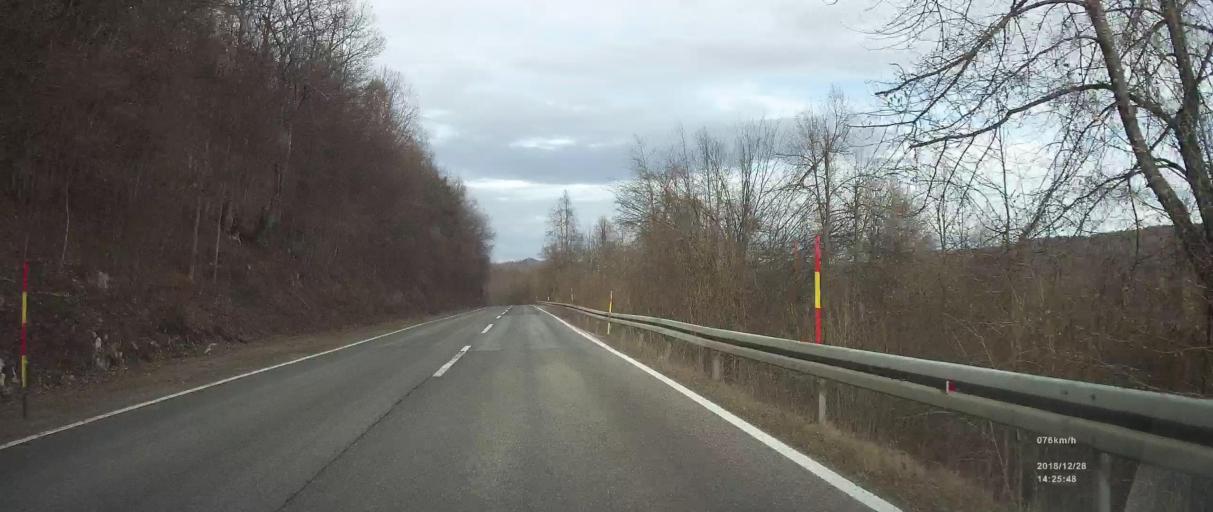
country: HR
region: Primorsko-Goranska
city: Vrbovsko
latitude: 45.3978
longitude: 15.1075
